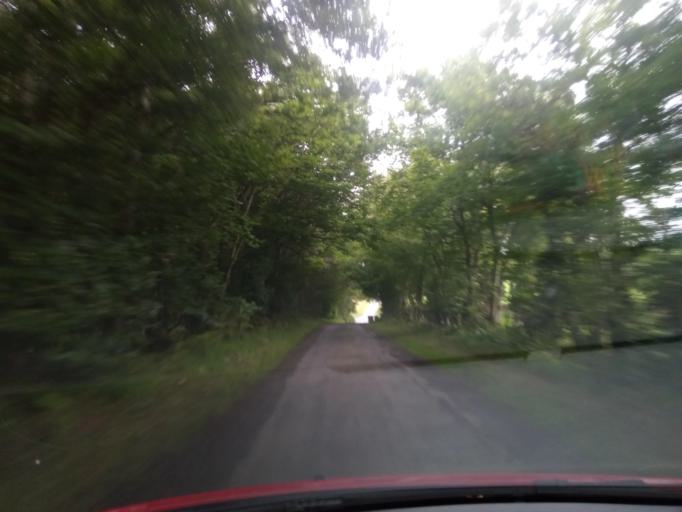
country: GB
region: Scotland
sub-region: The Scottish Borders
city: Galashiels
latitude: 55.6657
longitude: -2.8805
